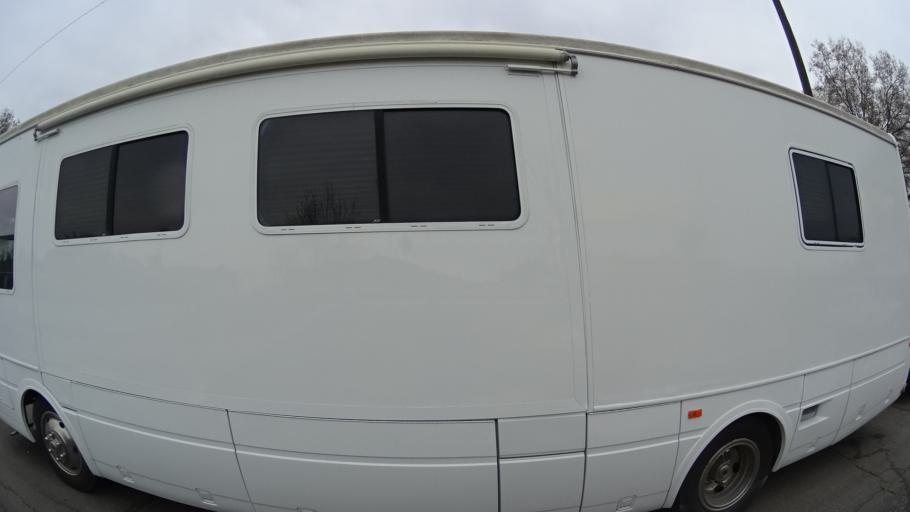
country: US
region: California
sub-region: Fresno County
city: Clovis
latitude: 36.8392
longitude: -119.7924
